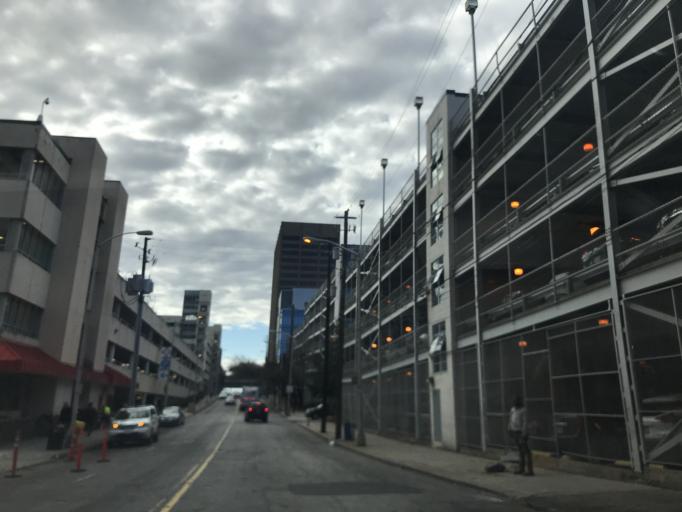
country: US
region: Georgia
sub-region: Fulton County
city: Atlanta
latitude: 33.7518
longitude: -84.3831
